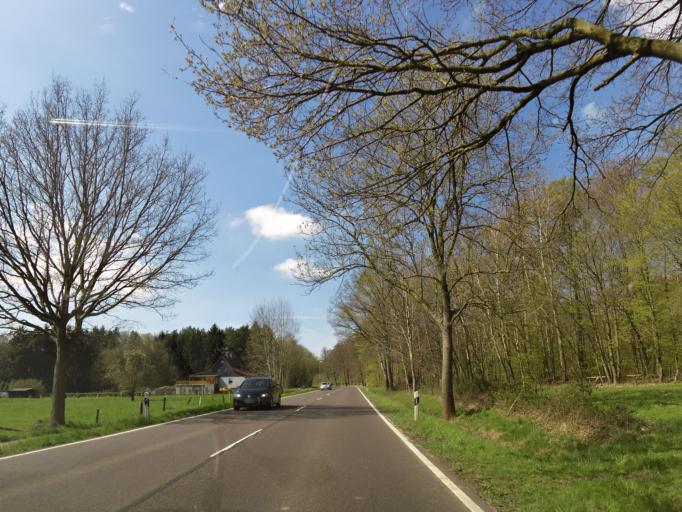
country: DE
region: Lower Saxony
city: Wolpinghausen
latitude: 52.4394
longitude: 9.2294
